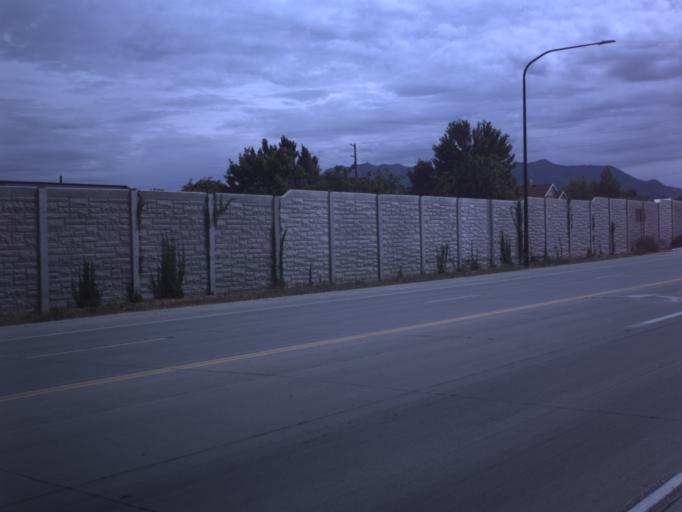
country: US
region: Utah
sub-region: Davis County
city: Clearfield
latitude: 41.1106
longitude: -112.0471
